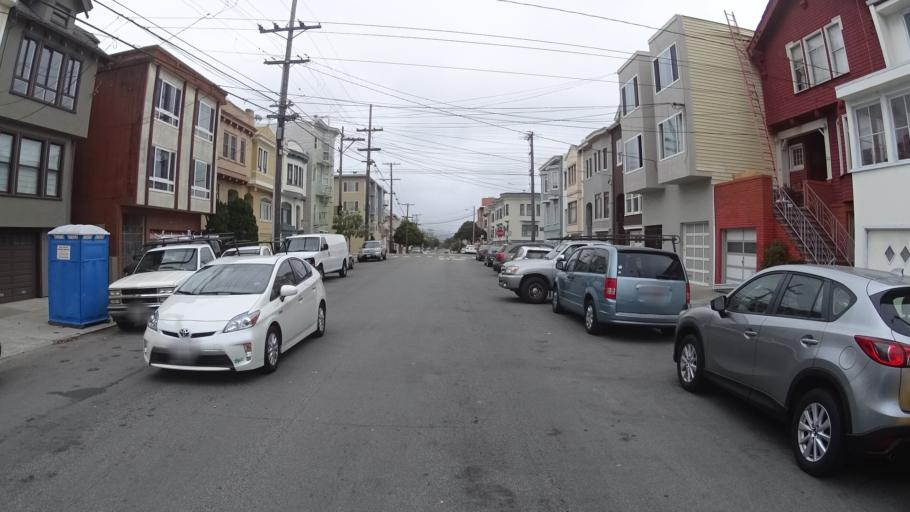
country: US
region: California
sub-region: San Francisco County
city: San Francisco
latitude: 37.7816
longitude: -122.4805
